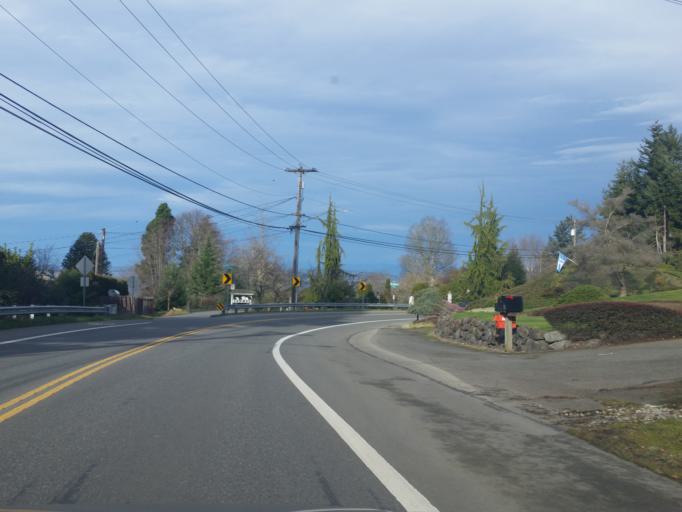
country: US
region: Washington
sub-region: Snohomish County
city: Mukilteo
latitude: 47.9560
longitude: -122.2610
